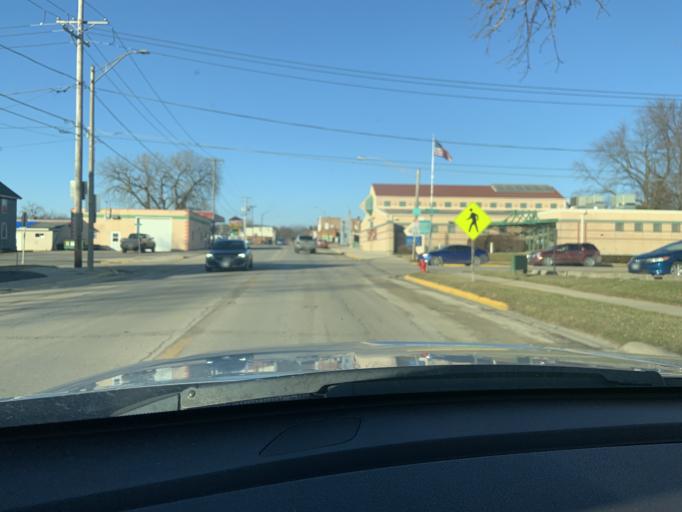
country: US
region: Illinois
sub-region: LaSalle County
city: Seneca
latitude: 41.3136
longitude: -88.6099
